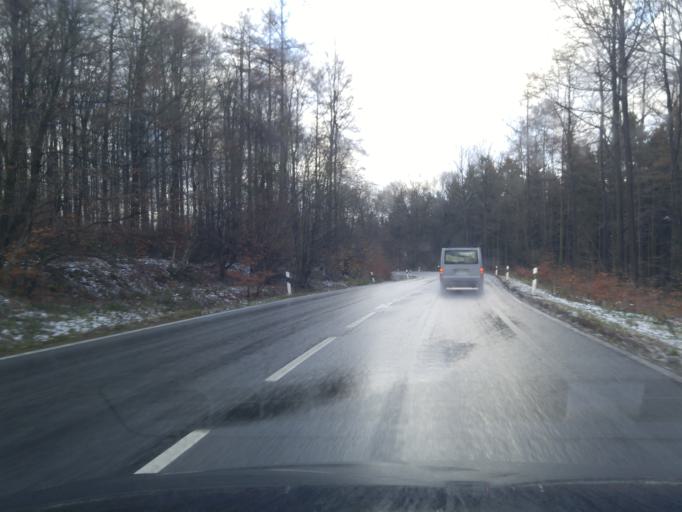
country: DE
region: Lower Saxony
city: Hannoversch Munden
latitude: 51.3810
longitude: 9.6333
